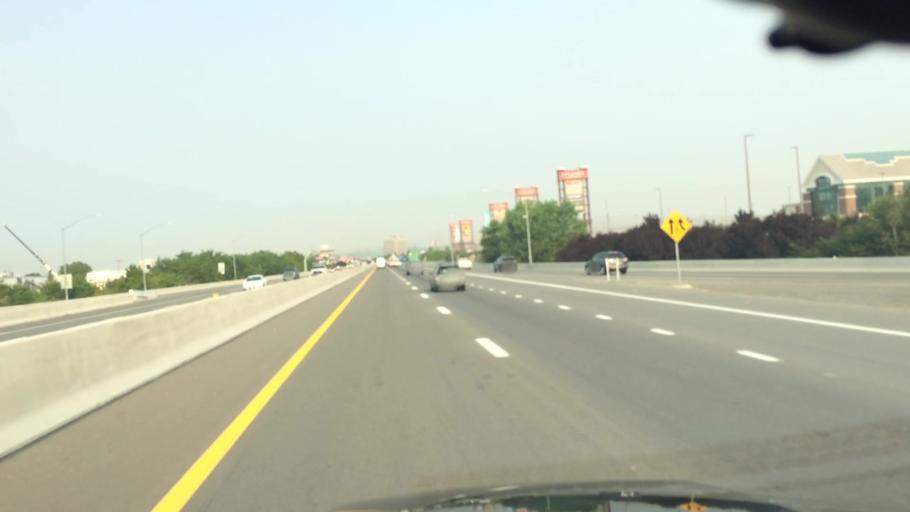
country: US
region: Nevada
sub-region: Washoe County
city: Sparks
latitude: 39.5286
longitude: -119.7189
